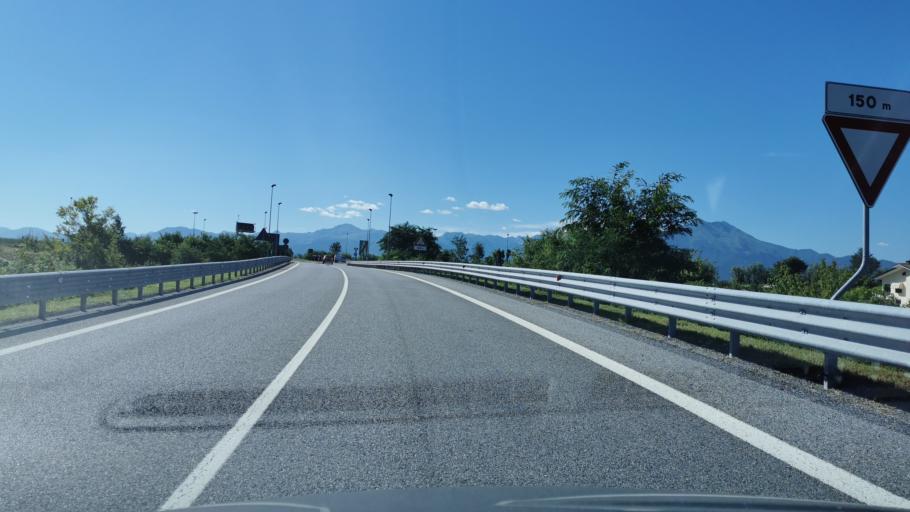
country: IT
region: Piedmont
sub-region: Provincia di Cuneo
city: Castelletto Stura
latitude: 44.4167
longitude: 7.5957
